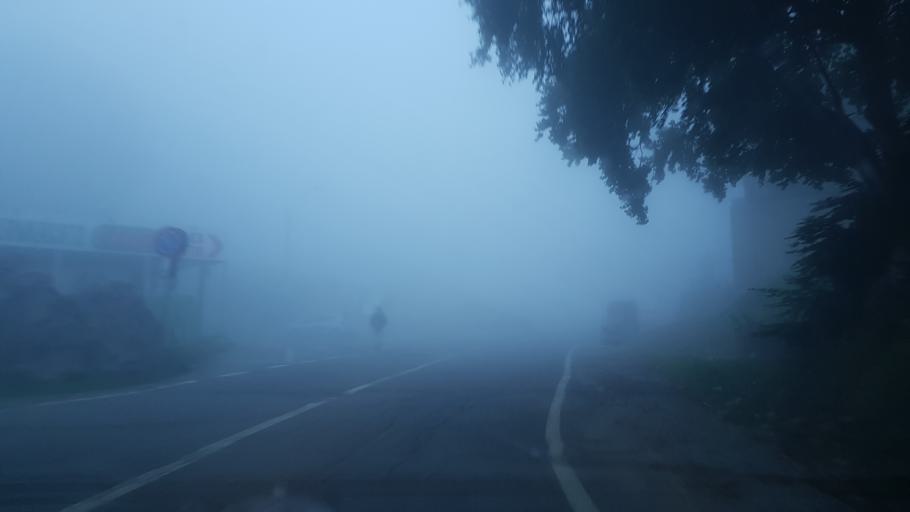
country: IT
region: Piedmont
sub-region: Provincia di Cuneo
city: Frabosa Soprana
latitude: 44.2539
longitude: 7.7799
